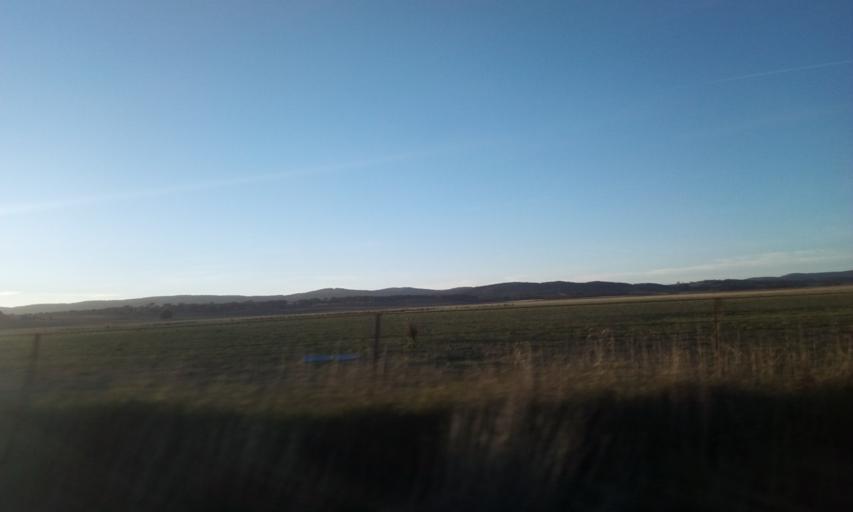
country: AU
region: New South Wales
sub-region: Goulburn Mulwaree
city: Goulburn
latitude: -34.8448
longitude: 149.5590
